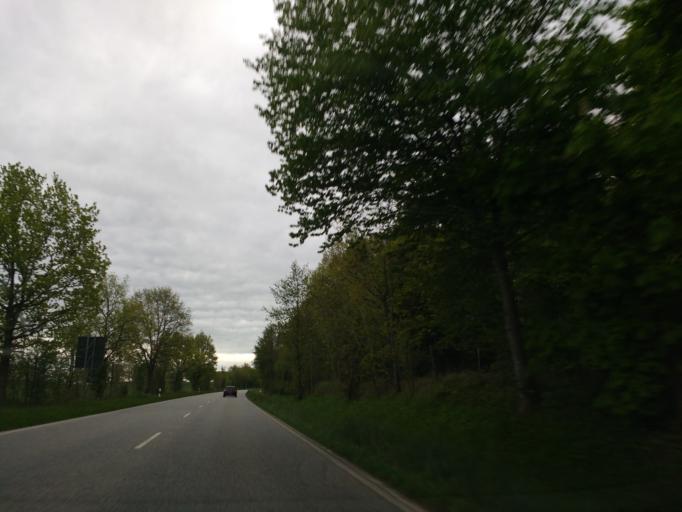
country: DE
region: Schleswig-Holstein
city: Damp
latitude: 54.5929
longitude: 9.9653
